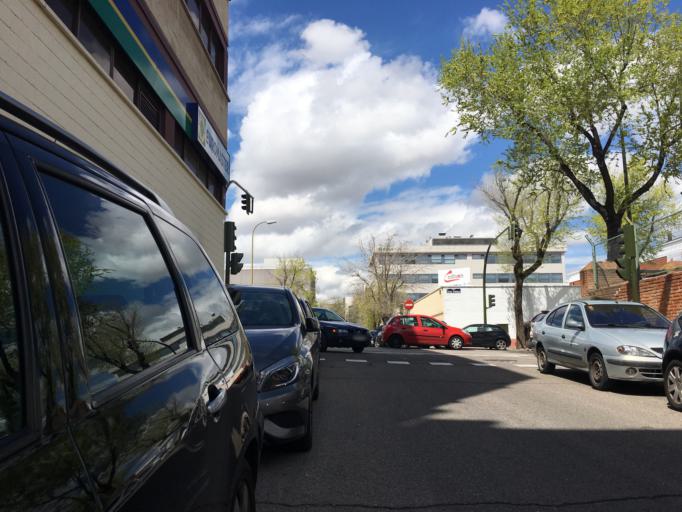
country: ES
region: Madrid
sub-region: Provincia de Madrid
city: San Blas
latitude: 40.4350
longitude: -3.6265
